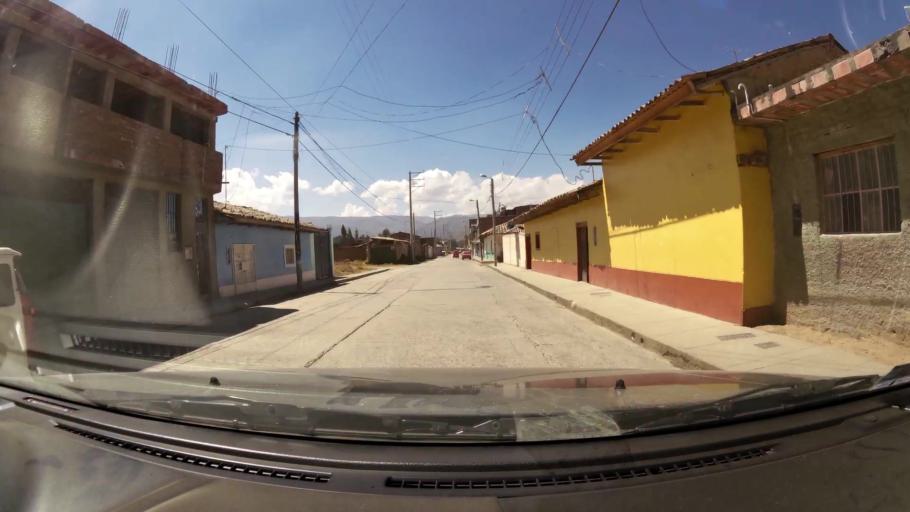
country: PE
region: Junin
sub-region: Provincia de Jauja
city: Jauja
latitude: -11.7749
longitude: -75.4947
